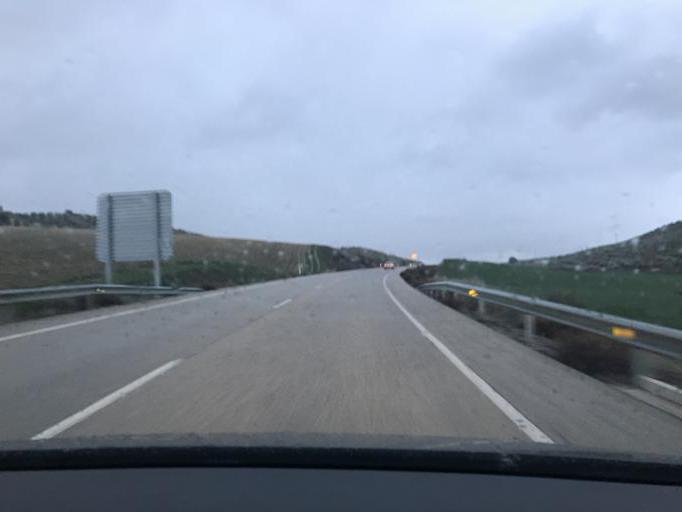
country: ES
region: Andalusia
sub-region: Provincia de Granada
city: Campotejar
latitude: 37.4686
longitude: -3.5872
